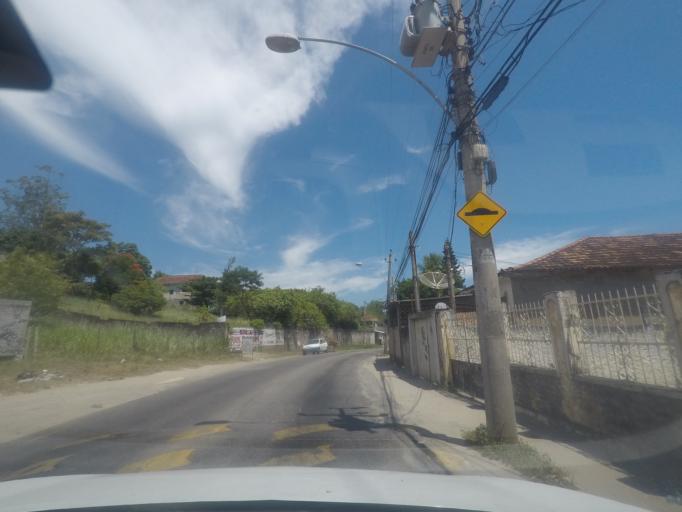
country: BR
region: Rio de Janeiro
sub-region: Itaguai
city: Itaguai
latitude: -22.9989
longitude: -43.6488
